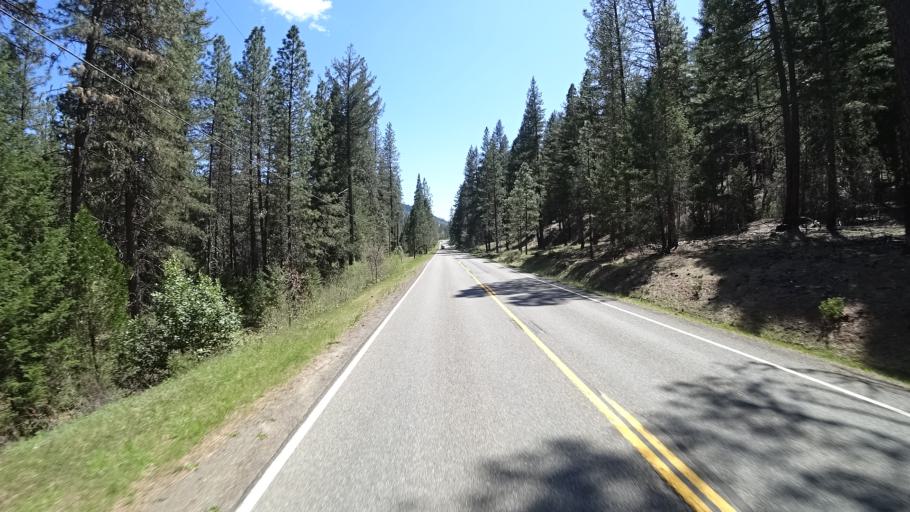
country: US
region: California
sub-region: Trinity County
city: Weaverville
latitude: 40.7602
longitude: -122.8873
